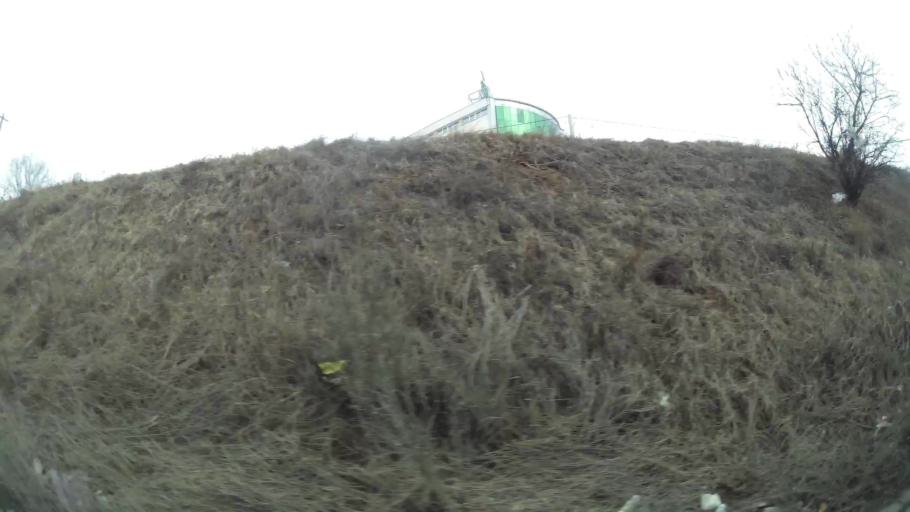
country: MK
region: Suto Orizari
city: Suto Orizare
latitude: 42.0305
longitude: 21.4059
